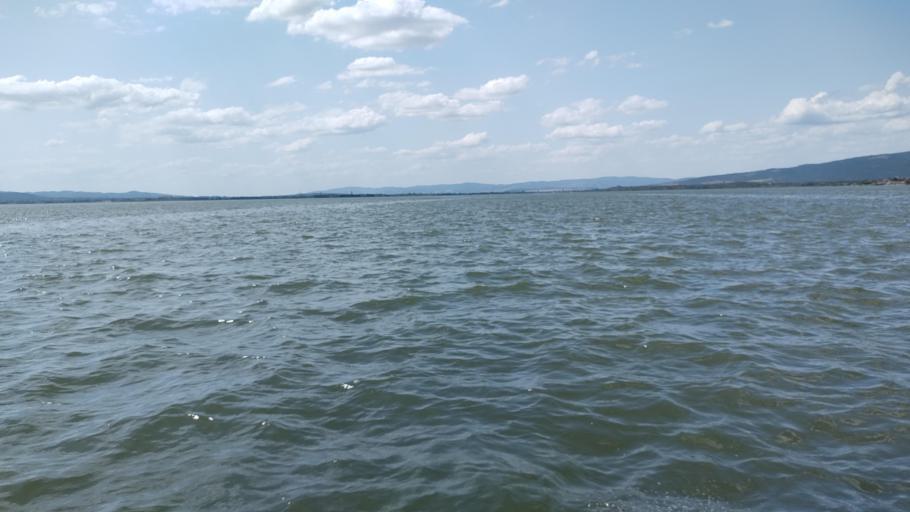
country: RO
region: Caras-Severin
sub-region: Comuna Pescari
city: Coronini
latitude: 44.6703
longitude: 21.6773
